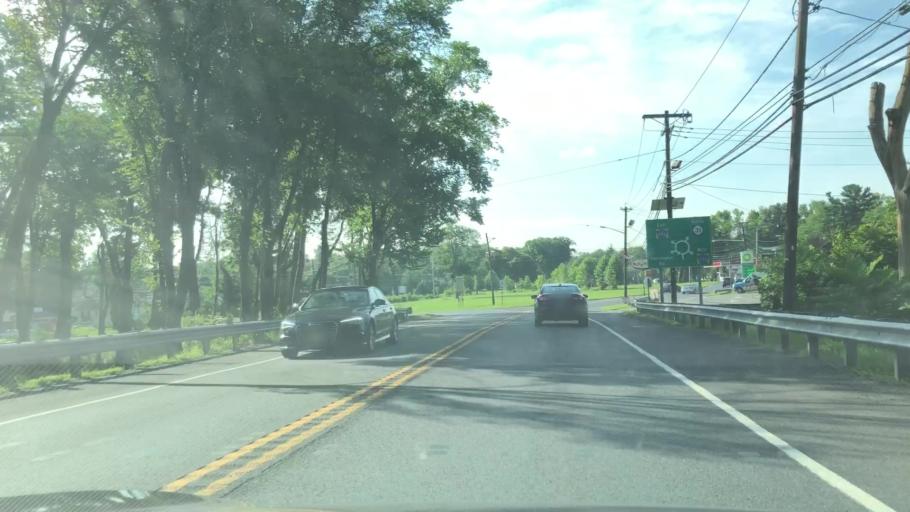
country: US
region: New Jersey
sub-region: Mercer County
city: Pennington
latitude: 40.3095
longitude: -74.7882
